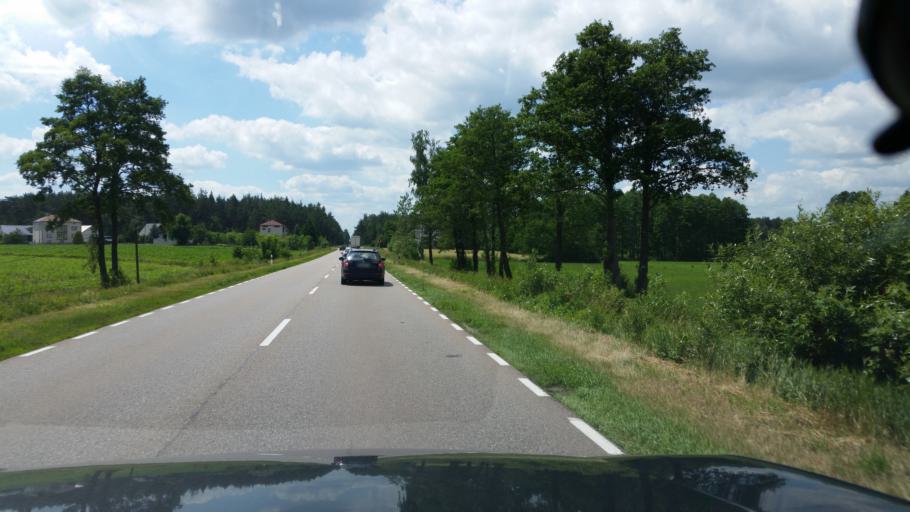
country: PL
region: Podlasie
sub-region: Powiat lomzynski
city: Sniadowo
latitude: 53.0324
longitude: 21.9754
